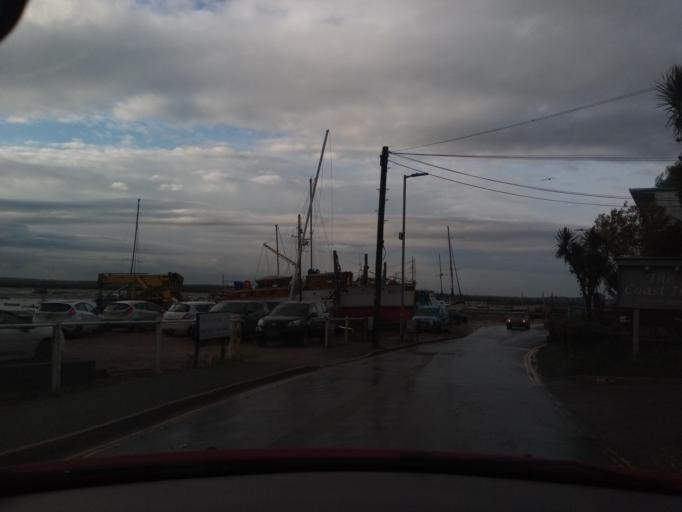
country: GB
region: England
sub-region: Essex
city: West Mersea
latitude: 51.7780
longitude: 0.8992
